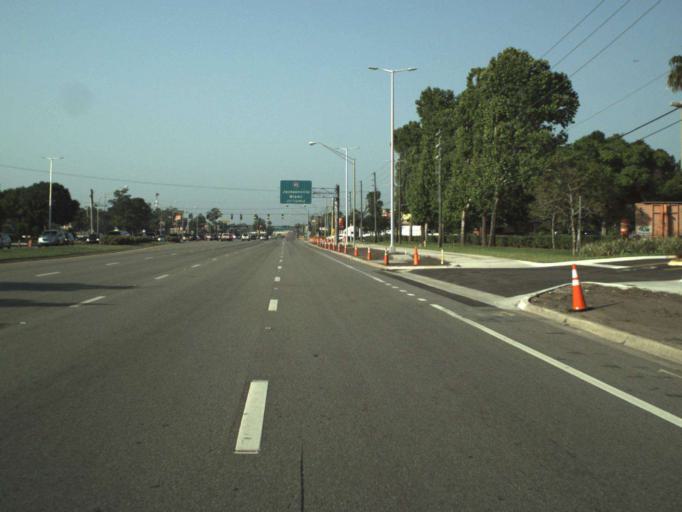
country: US
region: Florida
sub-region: Volusia County
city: Daytona Beach
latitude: 29.1840
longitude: -81.0783
